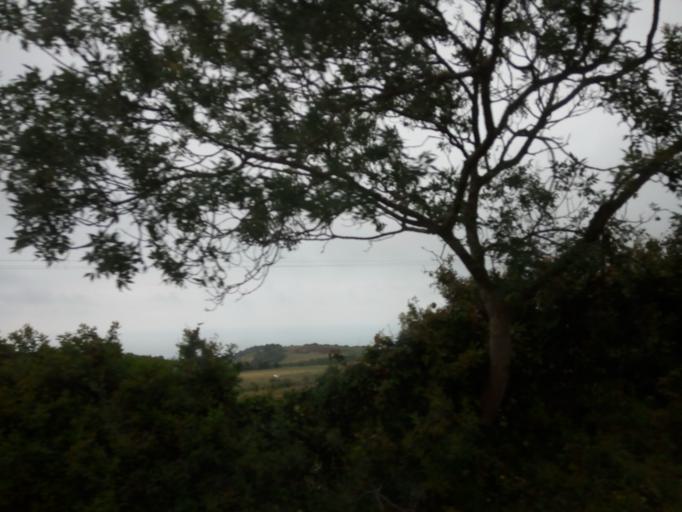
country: DZ
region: Tipaza
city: Tipasa
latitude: 36.5768
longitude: 2.5519
